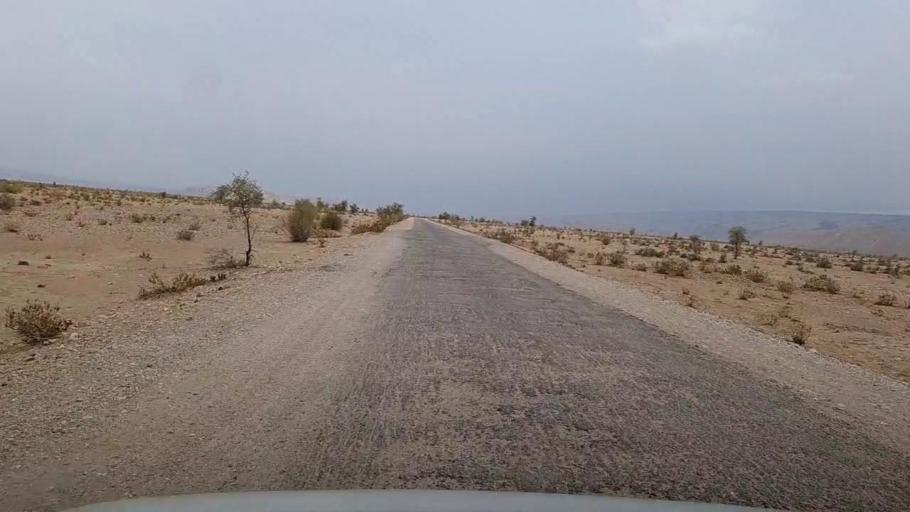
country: PK
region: Sindh
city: Sehwan
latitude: 26.2716
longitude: 67.7236
